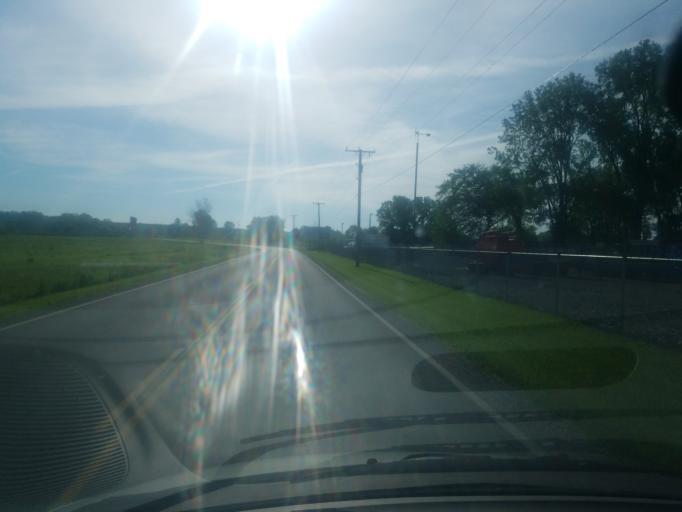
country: US
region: Ohio
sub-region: Marion County
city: Marion
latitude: 40.5999
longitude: -83.0917
